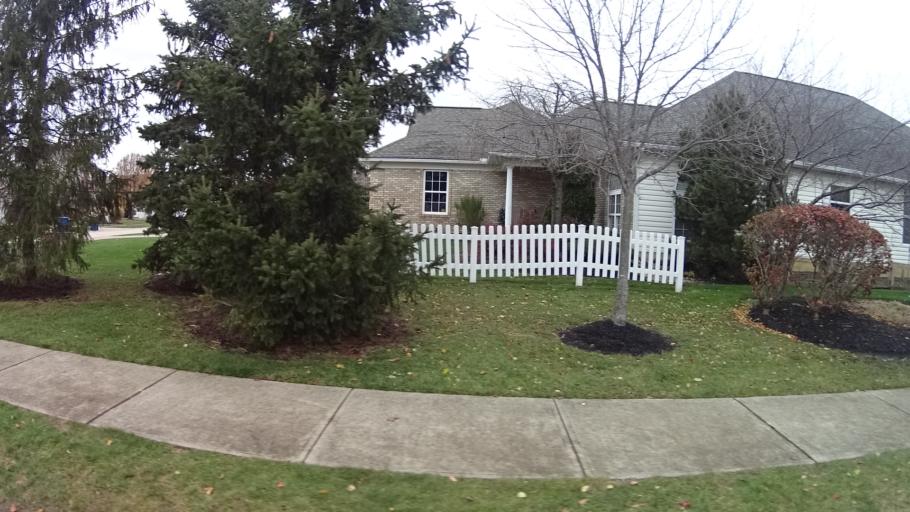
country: US
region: Ohio
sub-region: Lorain County
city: North Ridgeville
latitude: 41.3546
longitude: -82.0387
